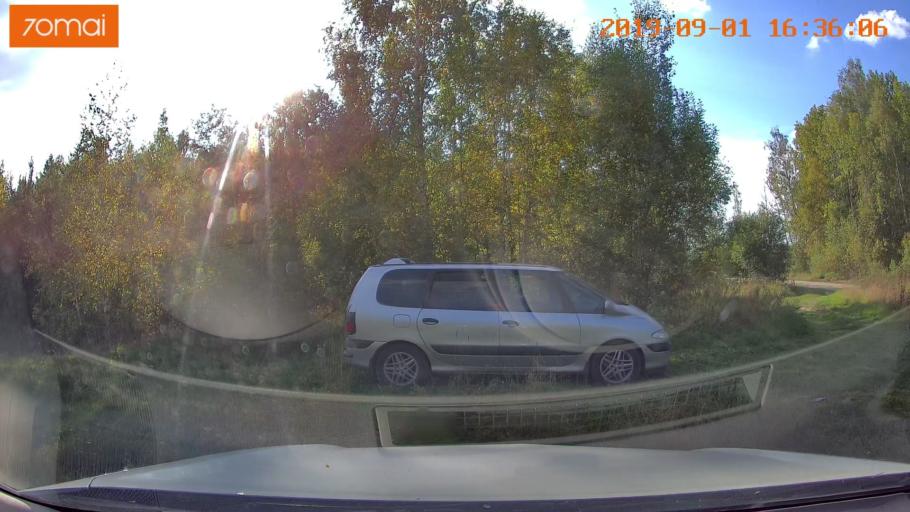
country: RU
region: Kaluga
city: Maloyaroslavets
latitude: 54.9477
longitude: 36.4767
